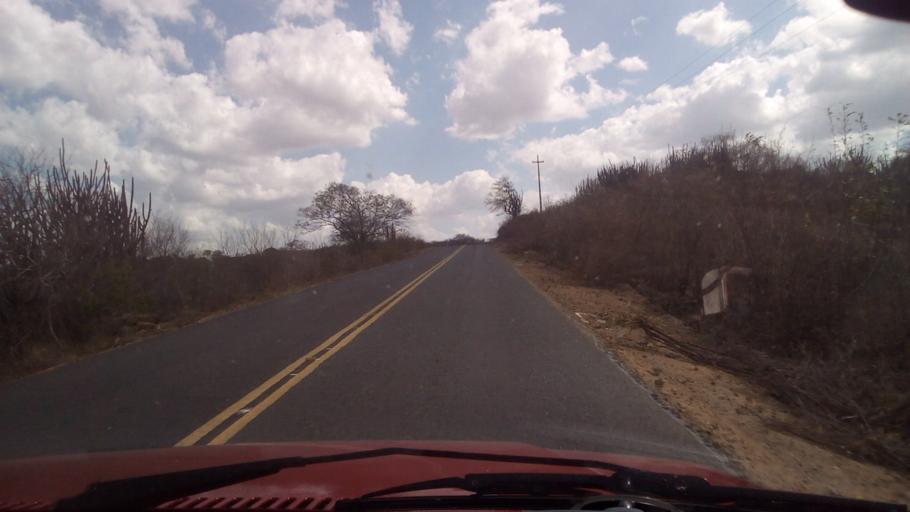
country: BR
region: Paraiba
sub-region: Cacimba De Dentro
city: Cacimba de Dentro
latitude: -6.6882
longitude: -35.7442
